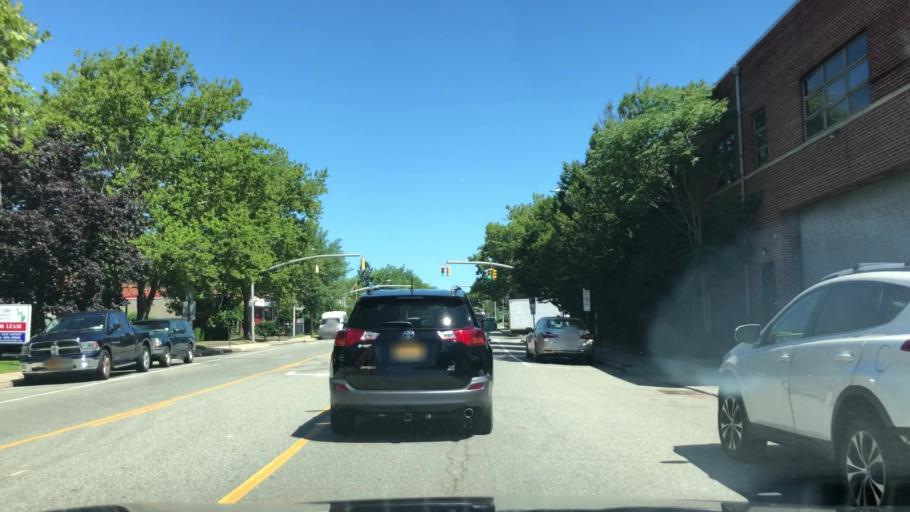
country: US
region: New York
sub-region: Nassau County
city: Rockville Centre
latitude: 40.6604
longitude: -73.6498
